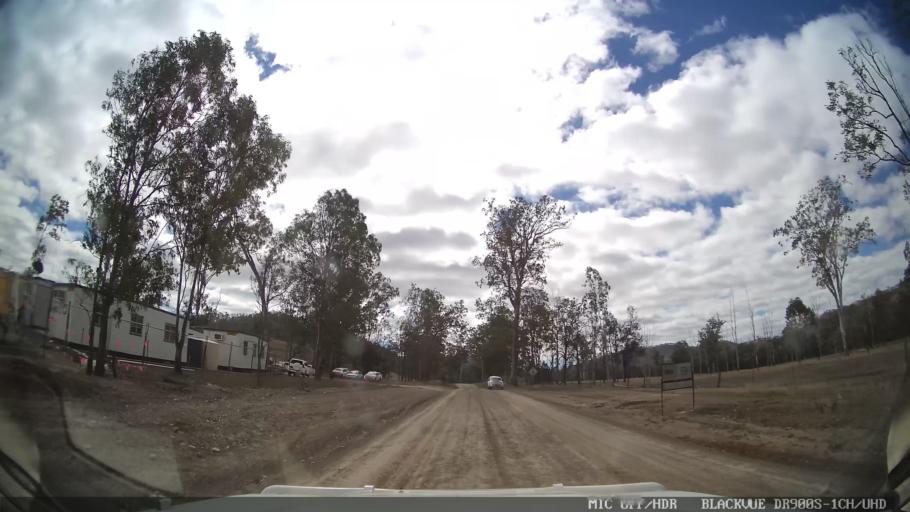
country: AU
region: Queensland
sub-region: Gladstone
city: Toolooa
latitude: -24.6127
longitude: 151.3005
